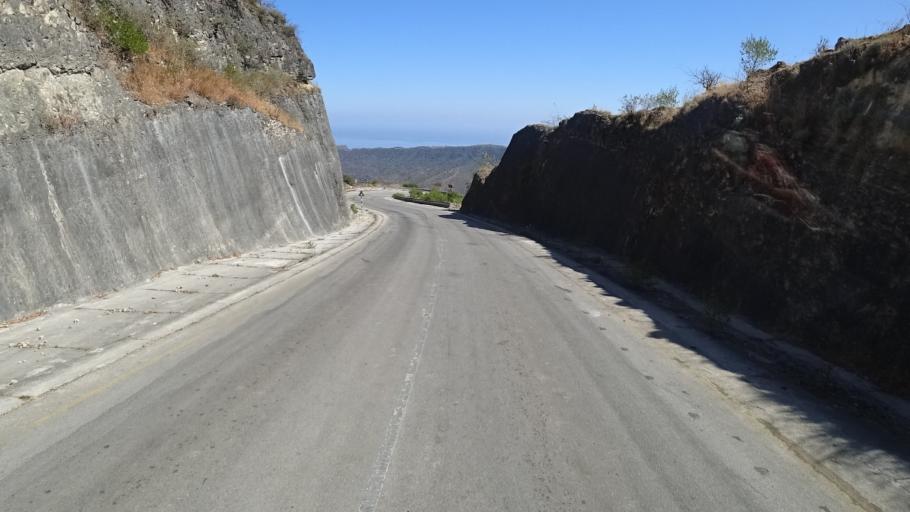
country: YE
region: Al Mahrah
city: Hawf
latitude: 16.7654
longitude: 53.3374
